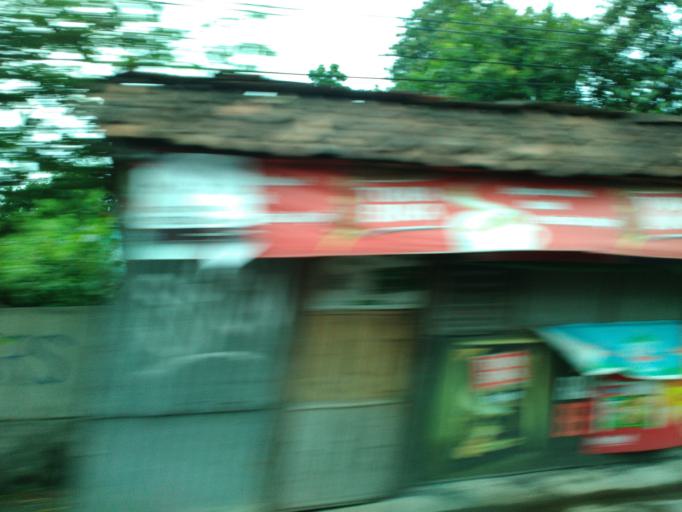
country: ID
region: Central Java
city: Gatak
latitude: -7.5806
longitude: 110.7147
